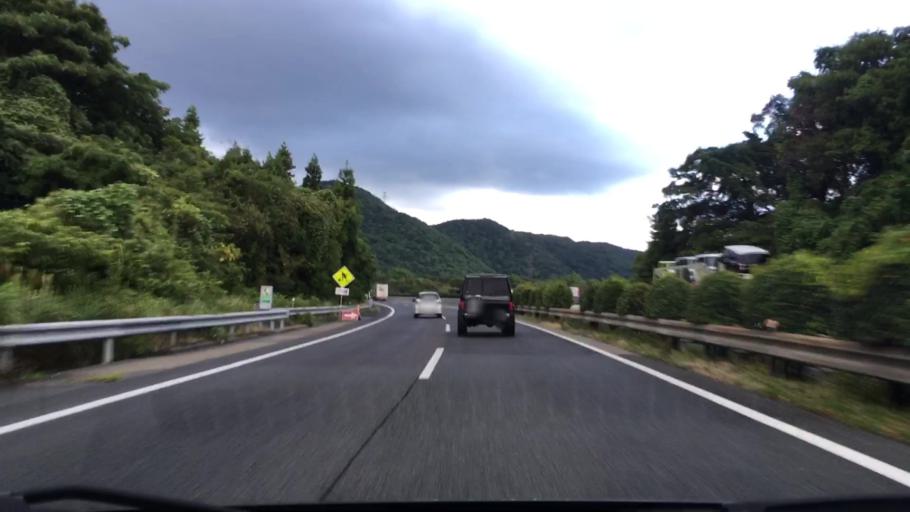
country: JP
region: Fukuoka
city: Kanda
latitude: 33.8554
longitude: 130.9378
